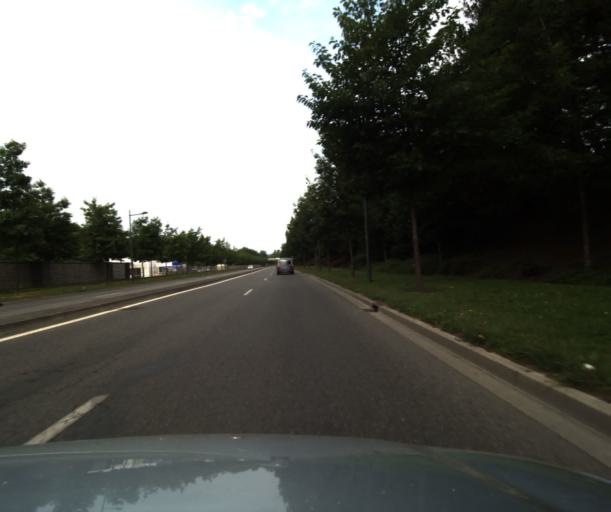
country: FR
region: Midi-Pyrenees
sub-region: Departement des Hautes-Pyrenees
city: Laloubere
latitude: 43.2223
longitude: 0.0546
